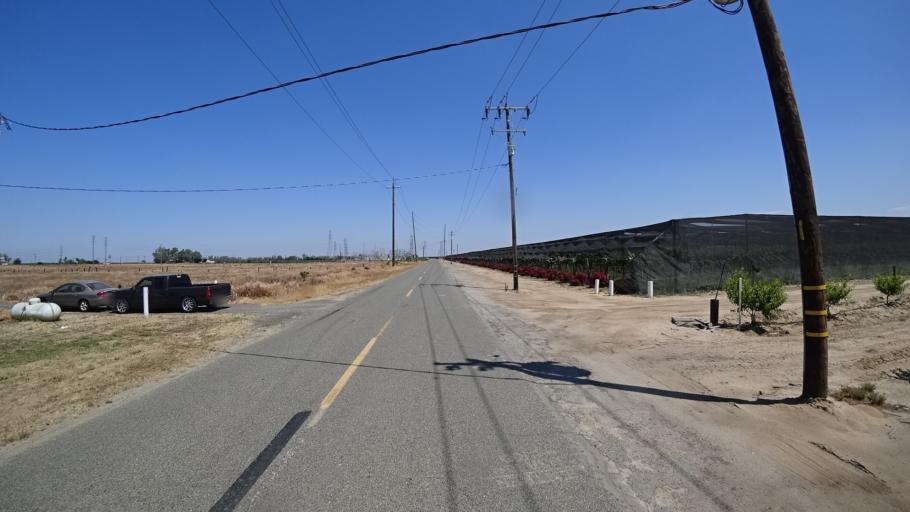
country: US
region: California
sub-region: Fresno County
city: Kingsburg
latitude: 36.4849
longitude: -119.5820
